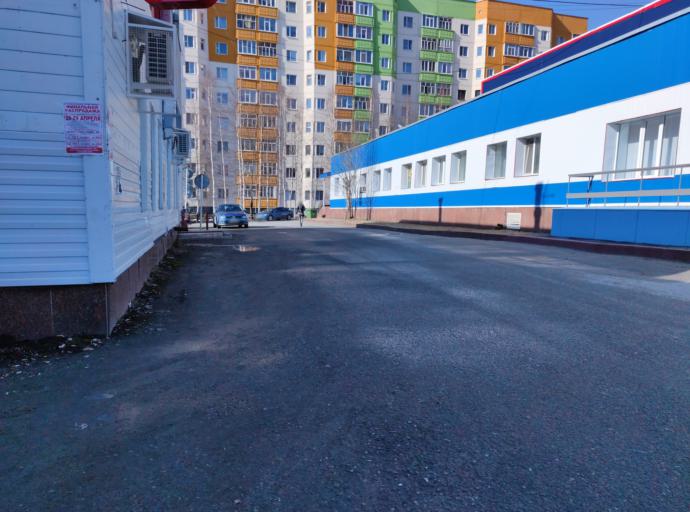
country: RU
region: Khanty-Mansiyskiy Avtonomnyy Okrug
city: Langepas
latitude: 61.2496
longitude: 75.1797
